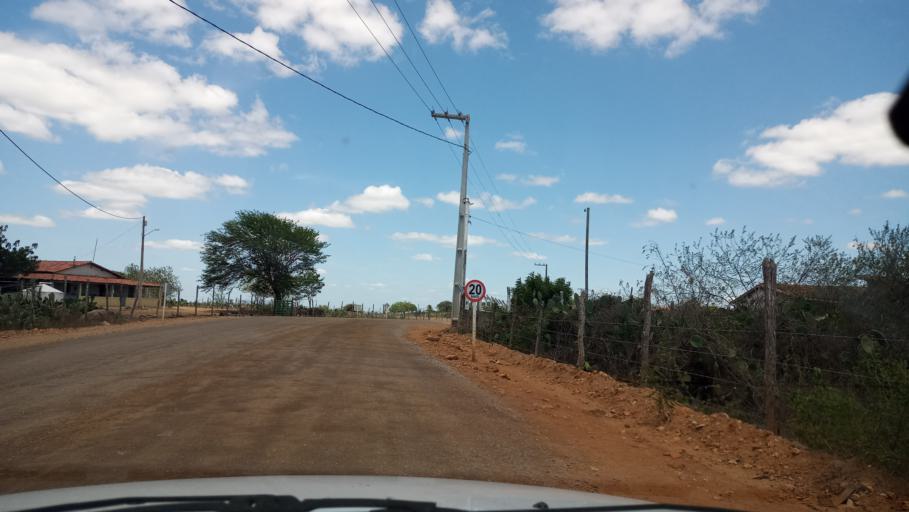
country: BR
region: Rio Grande do Norte
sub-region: Sao Paulo Do Potengi
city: Sao Paulo do Potengi
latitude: -5.7842
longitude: -35.9154
